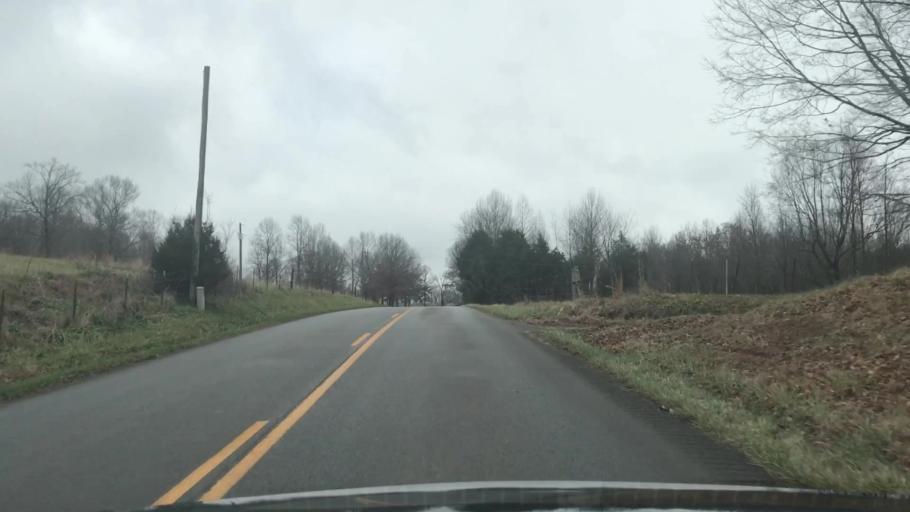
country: US
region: Kentucky
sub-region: Monroe County
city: Tompkinsville
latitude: 36.7570
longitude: -85.7222
